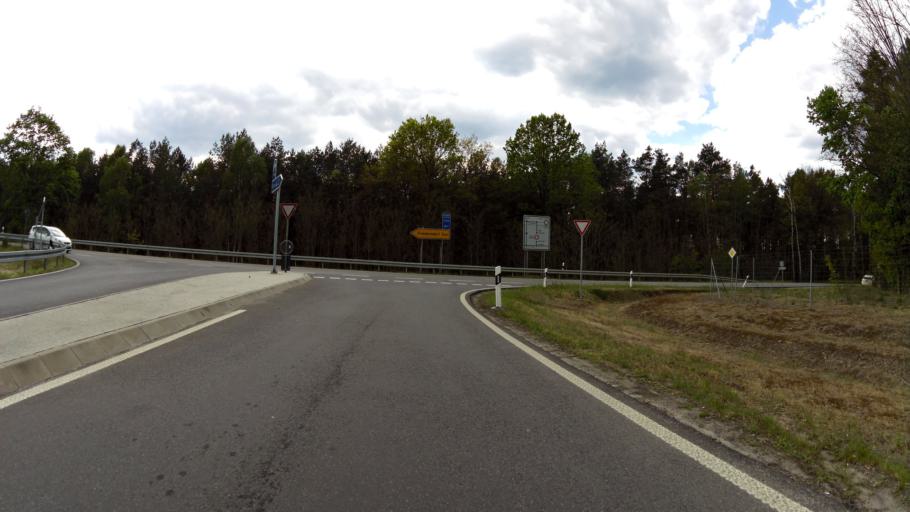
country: DE
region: Brandenburg
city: Erkner
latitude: 52.3219
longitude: 13.7791
